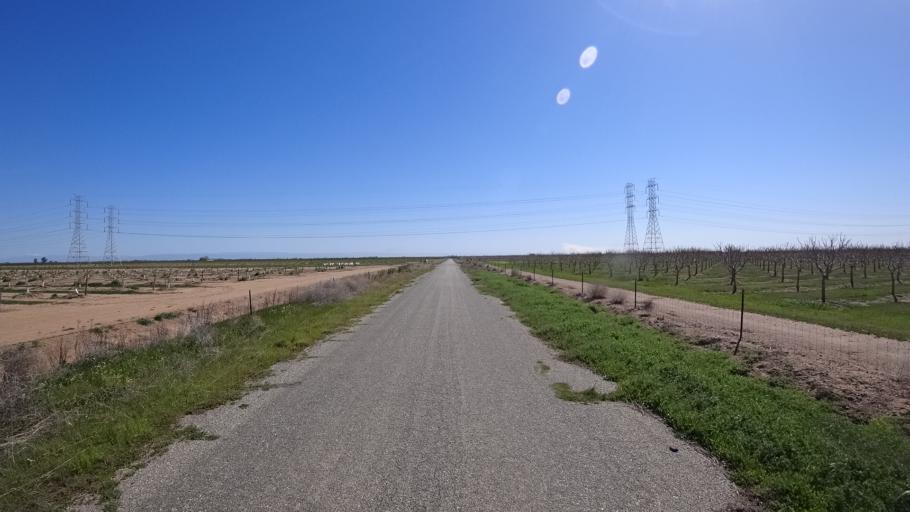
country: US
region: California
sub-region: Glenn County
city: Orland
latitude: 39.6539
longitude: -122.2663
